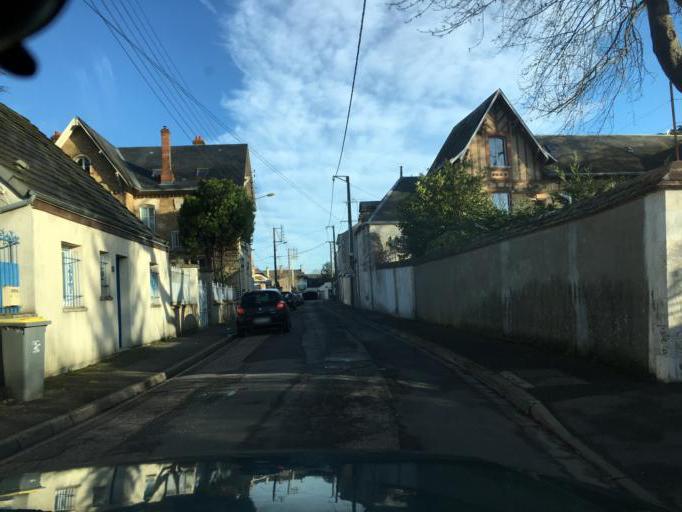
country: FR
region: Centre
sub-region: Departement du Loiret
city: Saint-Jean-le-Blanc
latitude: 47.9035
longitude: 1.9298
